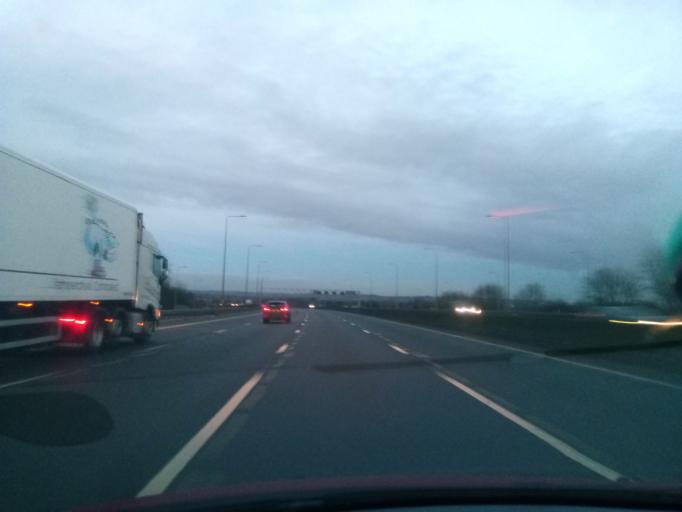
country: GB
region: England
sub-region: Nottinghamshire
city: Kimberley
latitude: 52.9856
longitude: -1.2398
